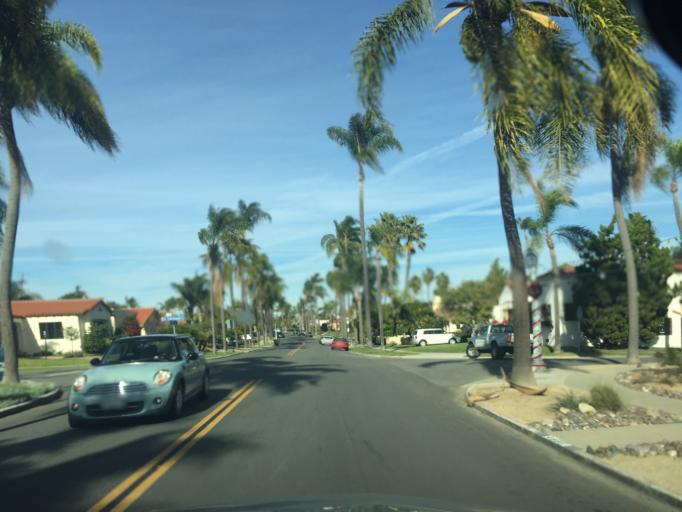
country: US
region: California
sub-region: San Diego County
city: San Diego
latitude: 32.7664
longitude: -117.1063
